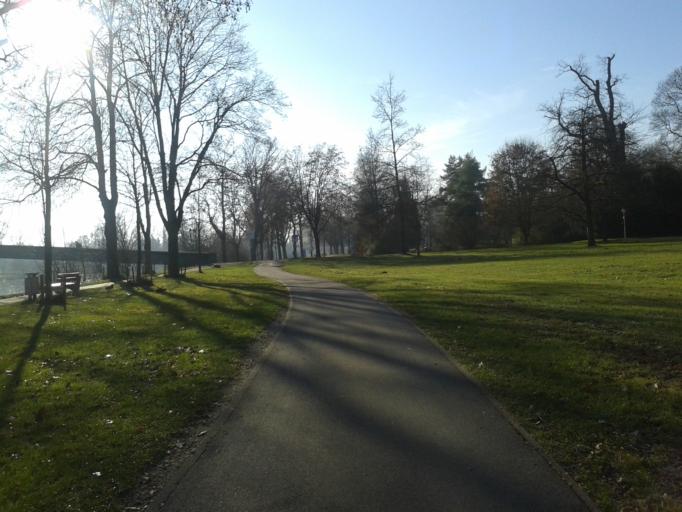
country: DE
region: Bavaria
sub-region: Swabia
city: Neu-Ulm
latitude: 48.4081
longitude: 10.0161
